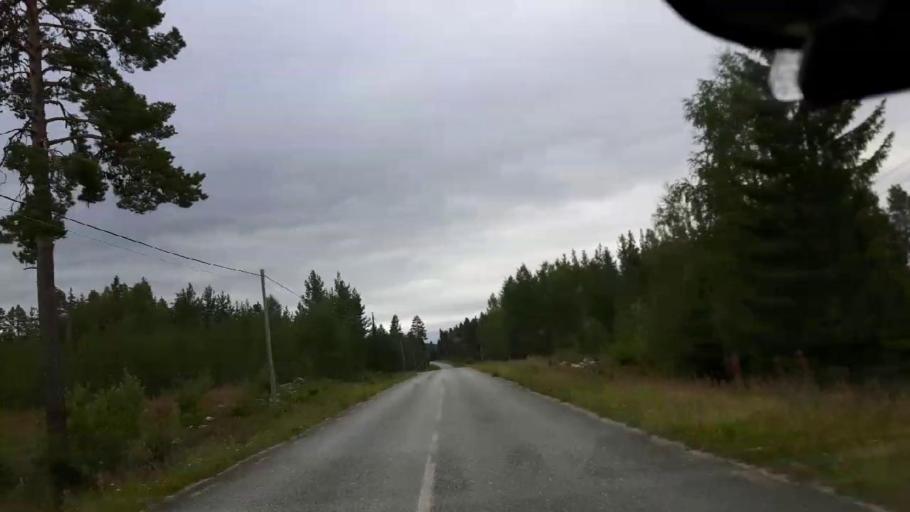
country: SE
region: Jaemtland
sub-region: Braecke Kommun
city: Braecke
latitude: 62.8818
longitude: 15.6183
